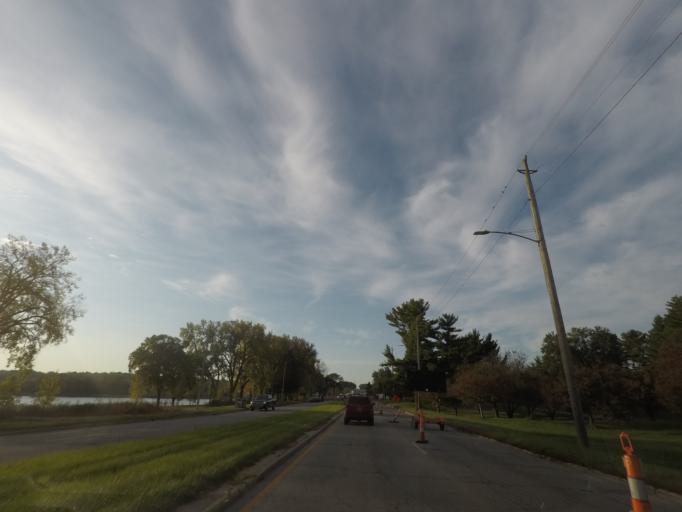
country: US
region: Iowa
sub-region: Polk County
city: Des Moines
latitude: 41.5719
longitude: -93.6450
